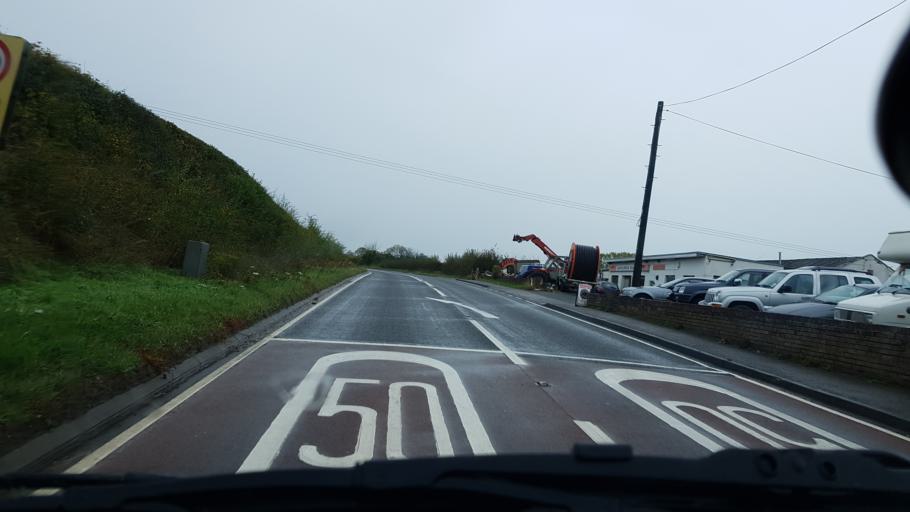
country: GB
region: England
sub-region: Worcestershire
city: Upton upon Severn
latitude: 52.0677
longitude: -2.1952
